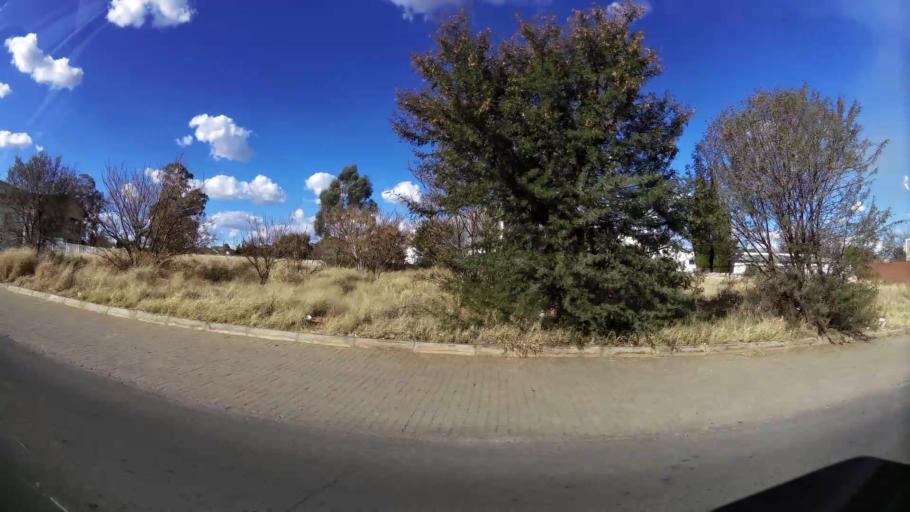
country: ZA
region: North-West
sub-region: Dr Kenneth Kaunda District Municipality
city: Klerksdorp
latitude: -26.8529
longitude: 26.6772
